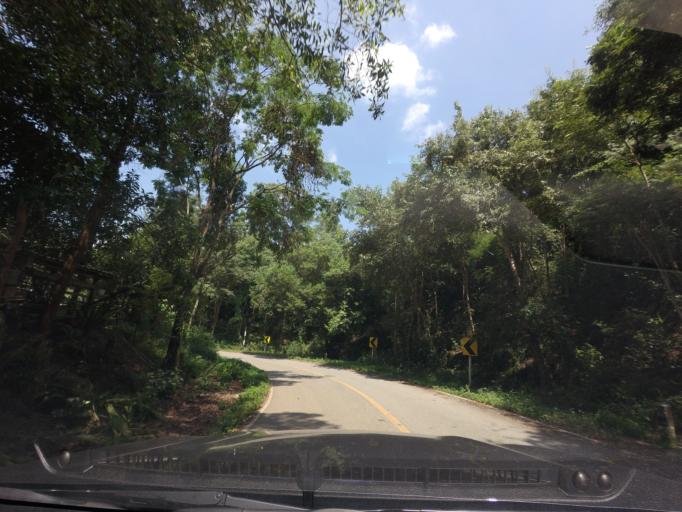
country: TH
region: Loei
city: Na Haeo
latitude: 17.6071
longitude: 100.8947
